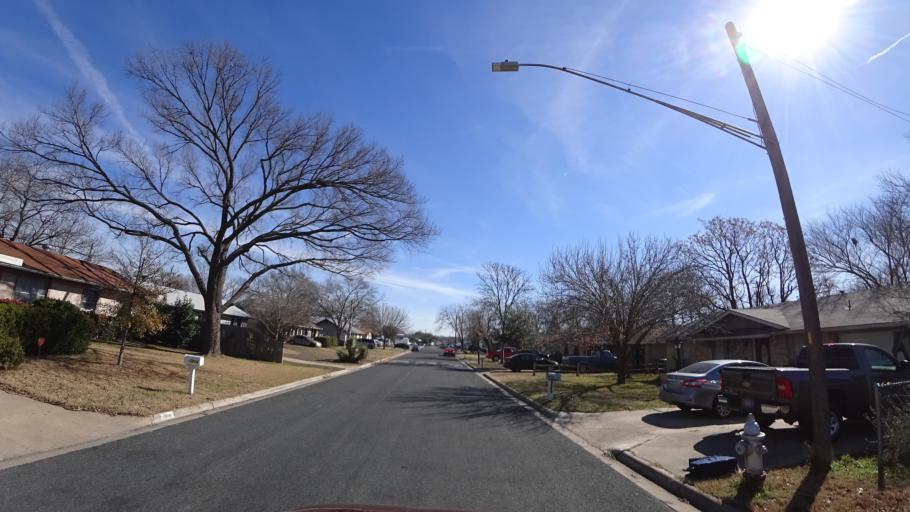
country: US
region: Texas
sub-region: Travis County
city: Wells Branch
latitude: 30.3760
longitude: -97.6963
